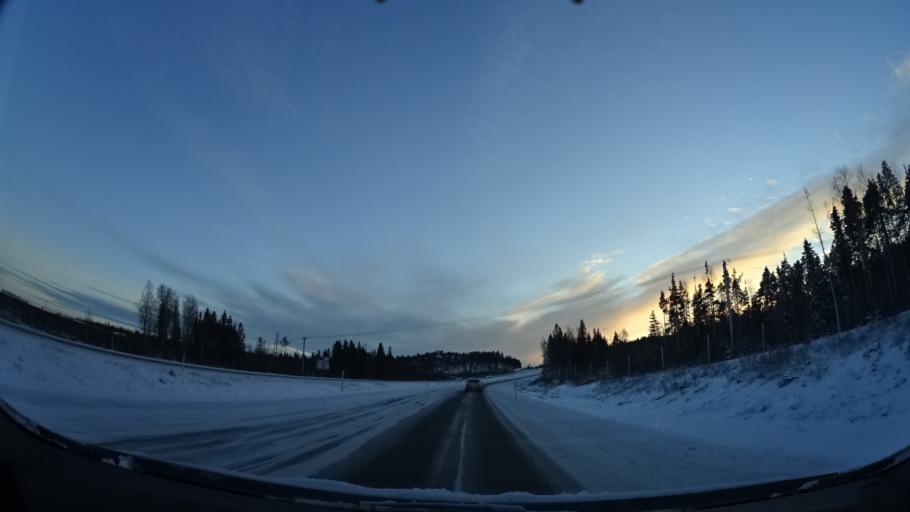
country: SE
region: Vaesterbotten
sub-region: Skelleftea Kommun
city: Kage
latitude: 64.8232
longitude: 21.0256
